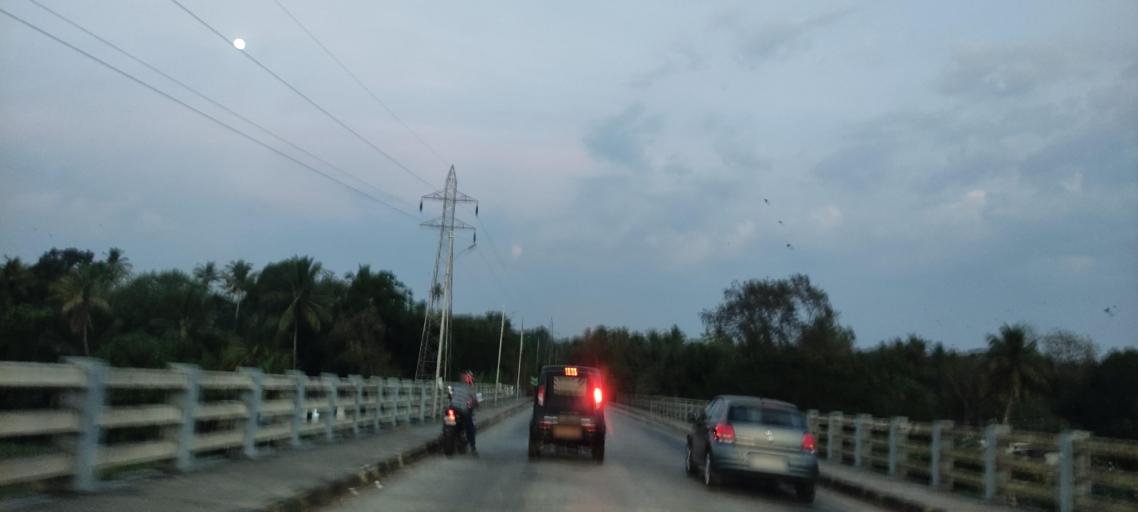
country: IN
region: Kerala
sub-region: Alappuzha
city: Kutiatodu
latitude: 9.7753
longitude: 76.3354
